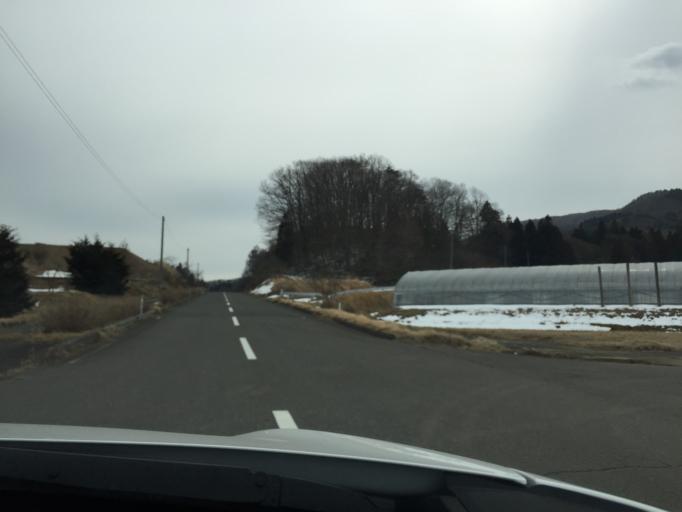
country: JP
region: Fukushima
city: Funehikimachi-funehiki
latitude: 37.3659
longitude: 140.5957
